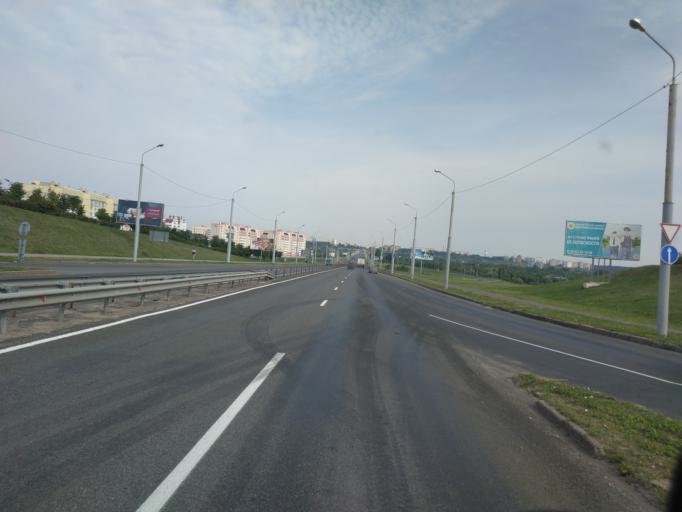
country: BY
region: Mogilev
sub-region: Mahilyowski Rayon
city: Veyno
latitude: 53.8796
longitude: 30.3832
